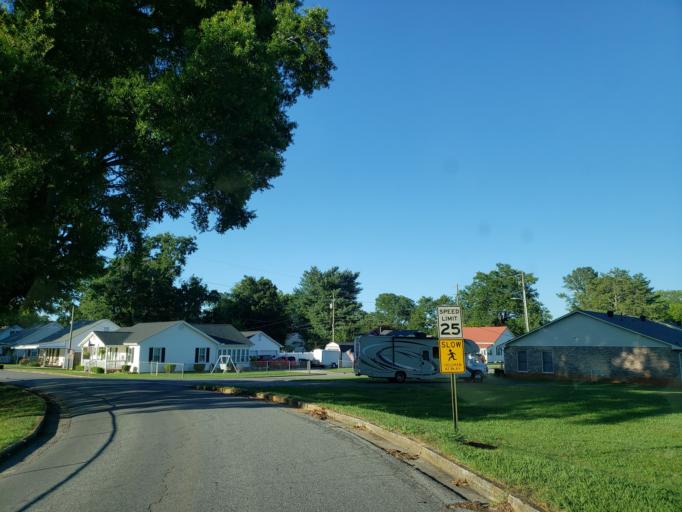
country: US
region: Georgia
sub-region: Polk County
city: Aragon
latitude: 34.0424
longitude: -85.0586
